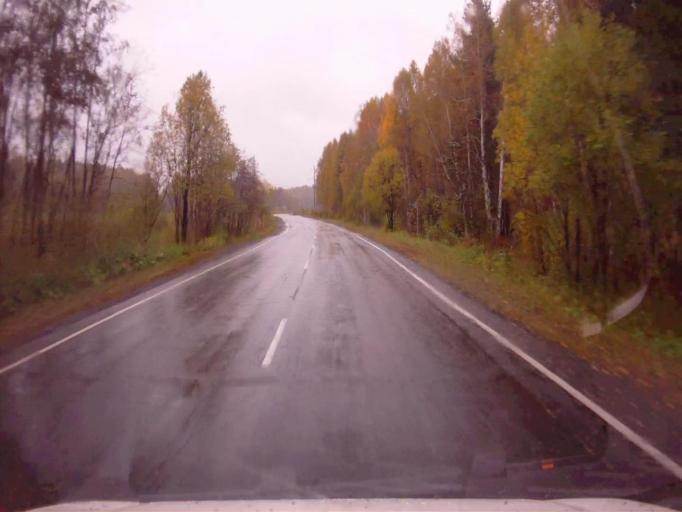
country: RU
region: Chelyabinsk
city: Verkhniy Ufaley
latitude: 55.9432
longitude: 60.4080
